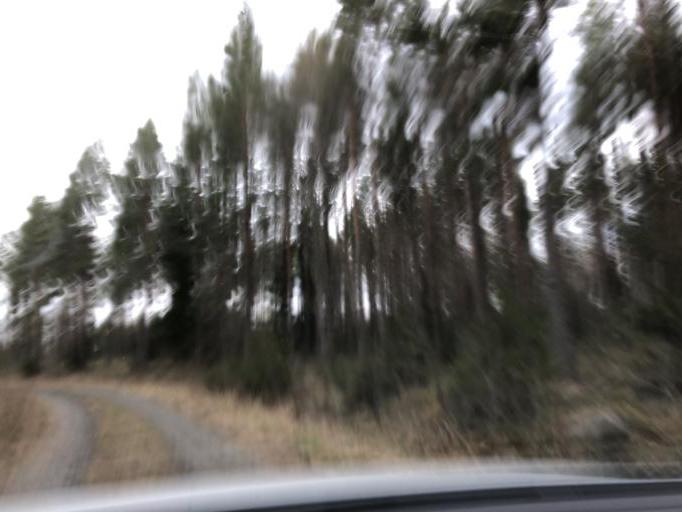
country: SE
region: Uppsala
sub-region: Heby Kommun
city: OEstervala
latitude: 60.3335
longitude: 17.1715
